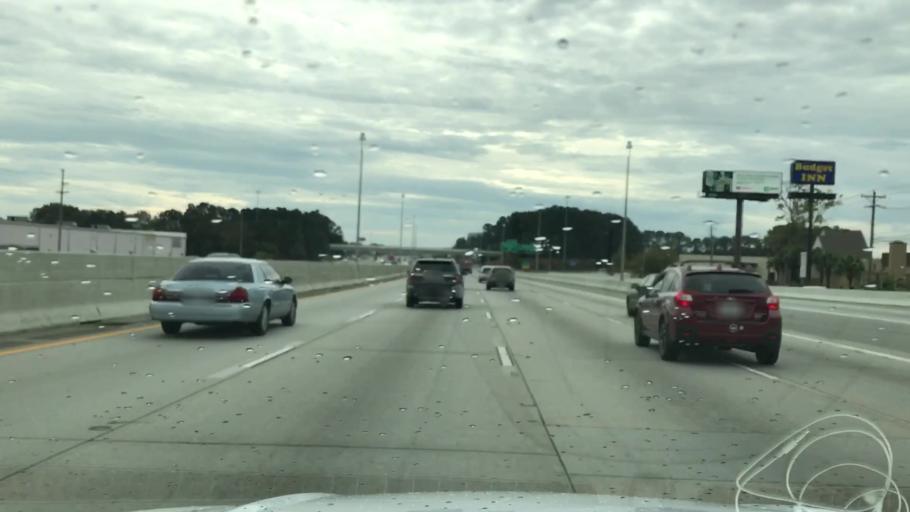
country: US
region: South Carolina
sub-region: Berkeley County
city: Hanahan
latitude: 32.9072
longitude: -80.0262
